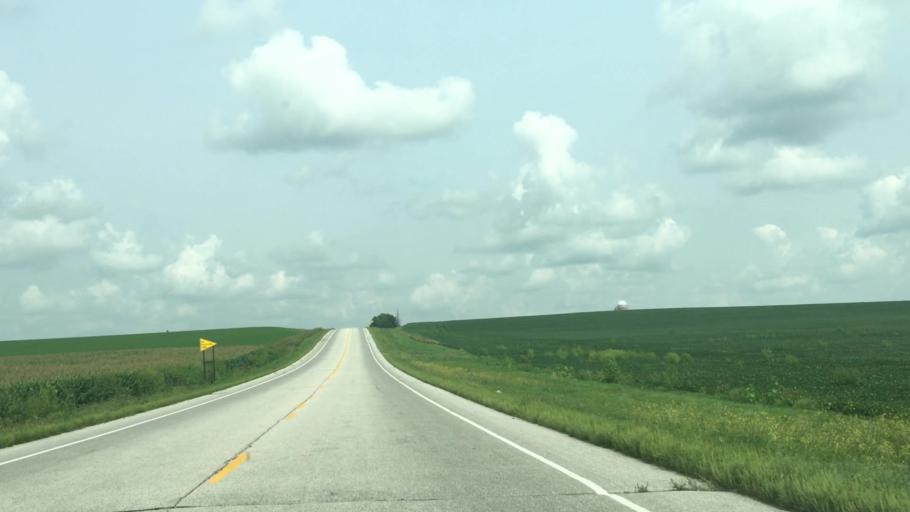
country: US
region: Minnesota
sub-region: Fillmore County
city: Harmony
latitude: 43.5968
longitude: -91.9297
